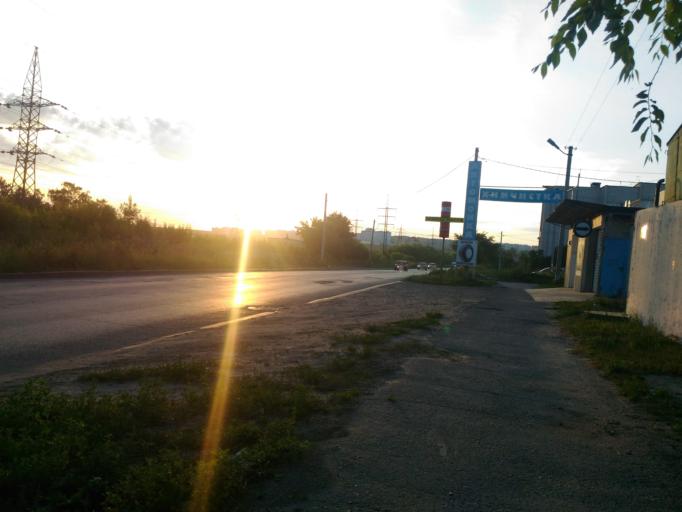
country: RU
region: Ulyanovsk
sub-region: Ulyanovskiy Rayon
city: Ulyanovsk
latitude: 54.3348
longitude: 48.3645
